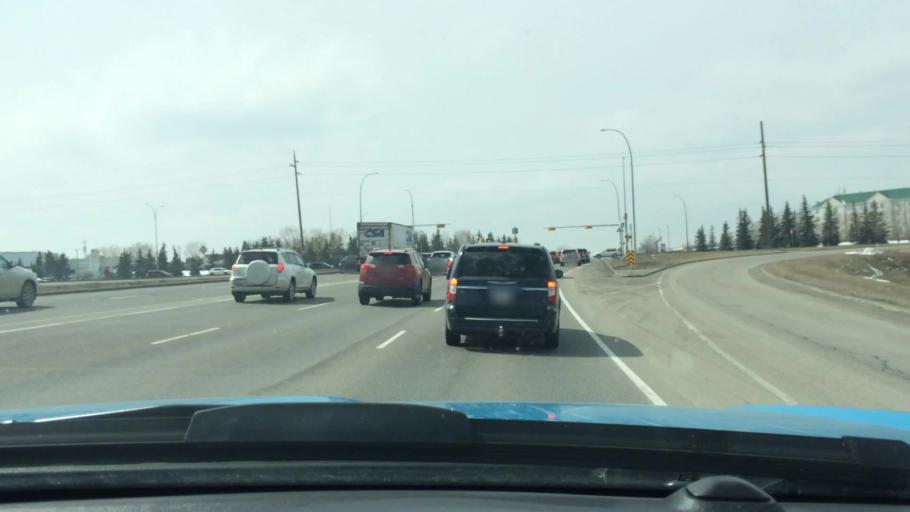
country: CA
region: Alberta
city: Calgary
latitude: 51.0930
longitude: -113.9995
